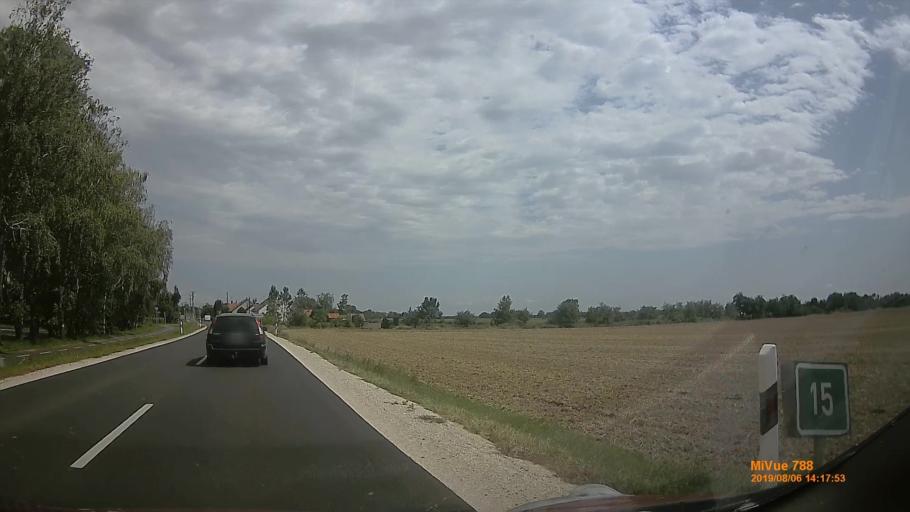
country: HU
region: Vas
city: Taplanszentkereszt
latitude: 47.1856
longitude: 16.7370
